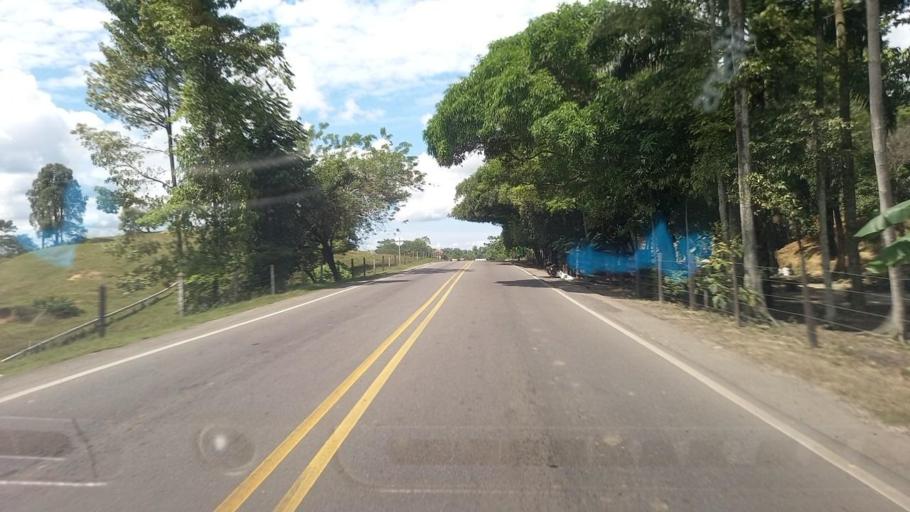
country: CO
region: Santander
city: Barrancabermeja
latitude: 7.1223
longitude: -73.5914
